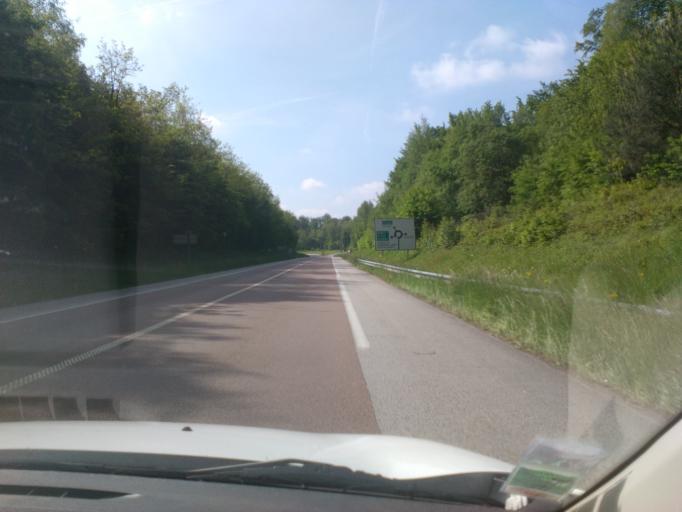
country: FR
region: Lorraine
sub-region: Departement des Vosges
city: Les Forges
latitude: 48.1939
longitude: 6.3996
